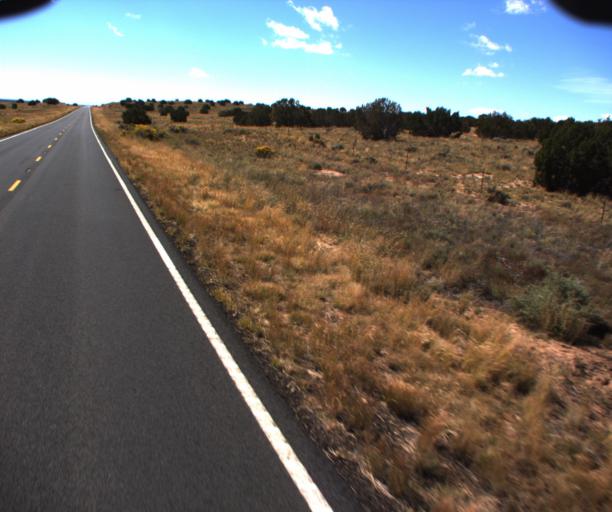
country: US
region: Arizona
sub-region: Apache County
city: Houck
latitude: 34.9588
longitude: -109.2290
